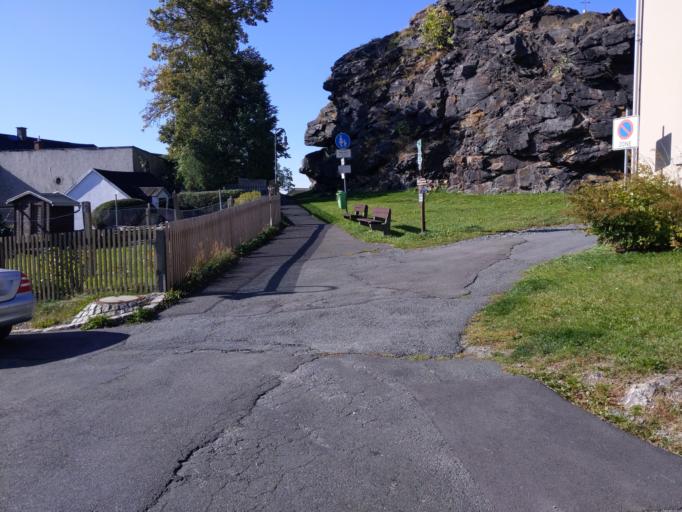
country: DE
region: Saxony
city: Pohl
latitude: 50.3917
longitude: 12.3296
